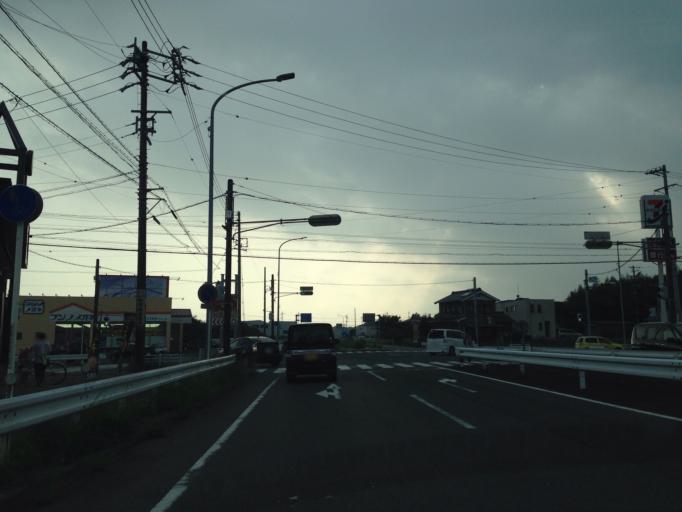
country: JP
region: Aichi
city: Shinshiro
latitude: 34.8911
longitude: 137.4732
